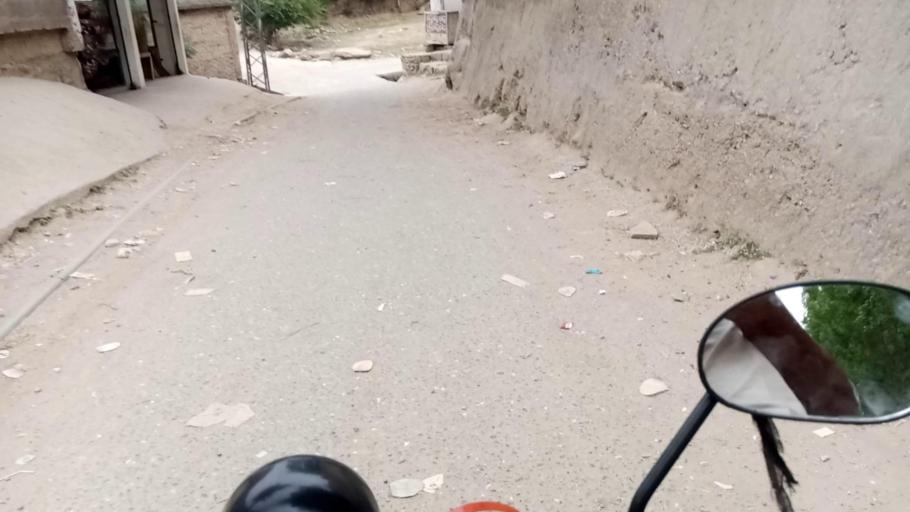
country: PK
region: Khyber Pakhtunkhwa
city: Saidu Sharif
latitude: 34.7513
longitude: 72.3778
